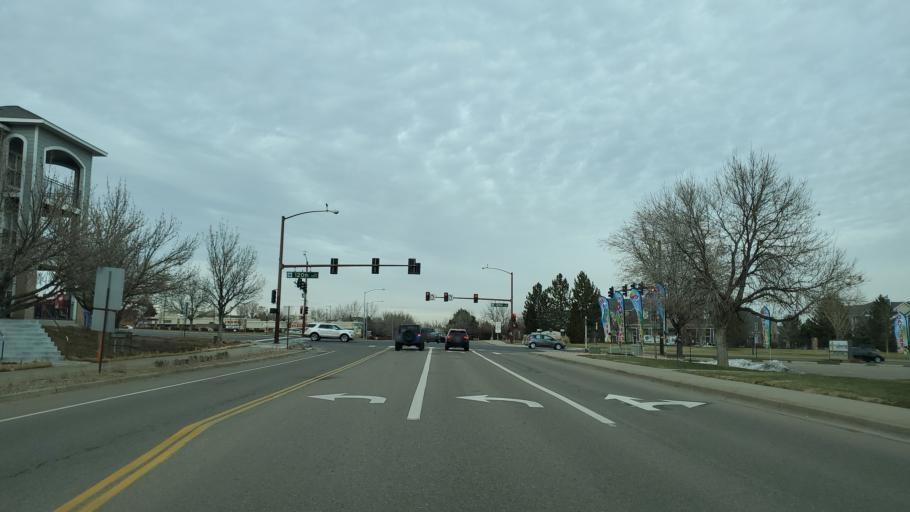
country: US
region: Colorado
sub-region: Adams County
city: Northglenn
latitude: 39.9131
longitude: -104.9533
